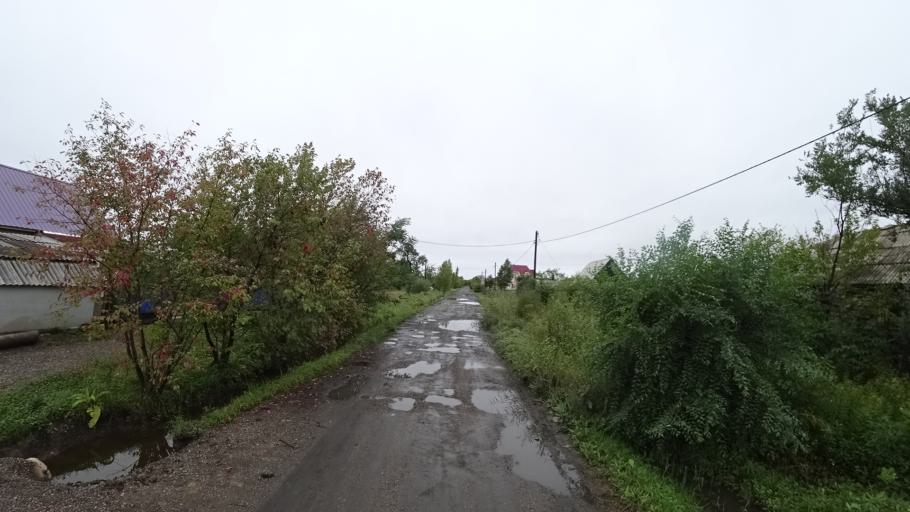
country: RU
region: Primorskiy
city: Monastyrishche
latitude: 44.2107
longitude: 132.4355
